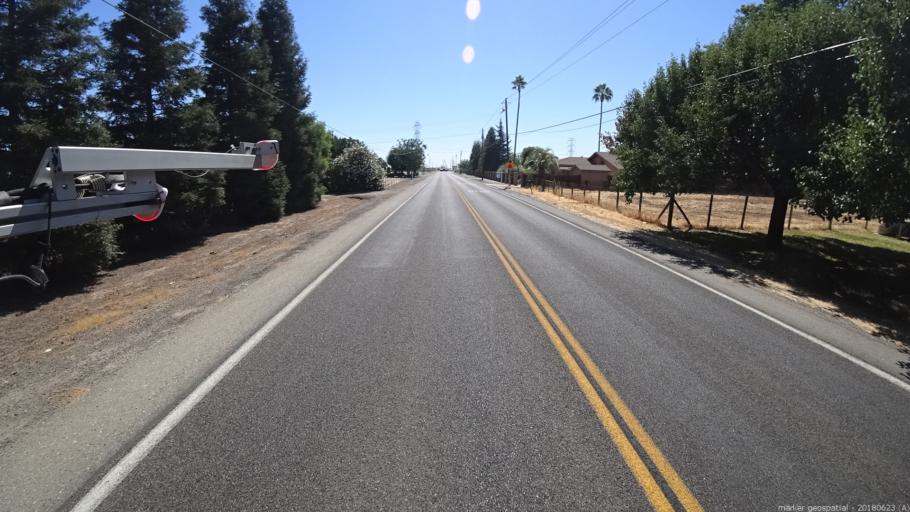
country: US
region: California
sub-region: Madera County
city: Parksdale
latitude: 36.9672
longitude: -120.0225
